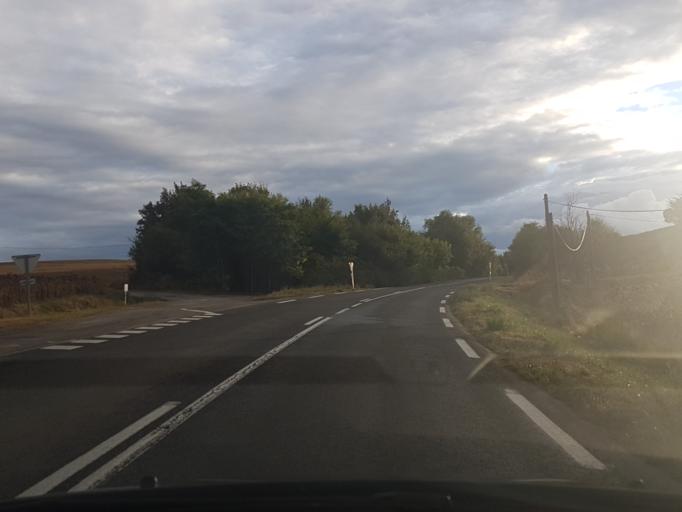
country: FR
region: Midi-Pyrenees
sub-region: Departement de l'Ariege
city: Mirepoix
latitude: 43.1544
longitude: 1.9792
